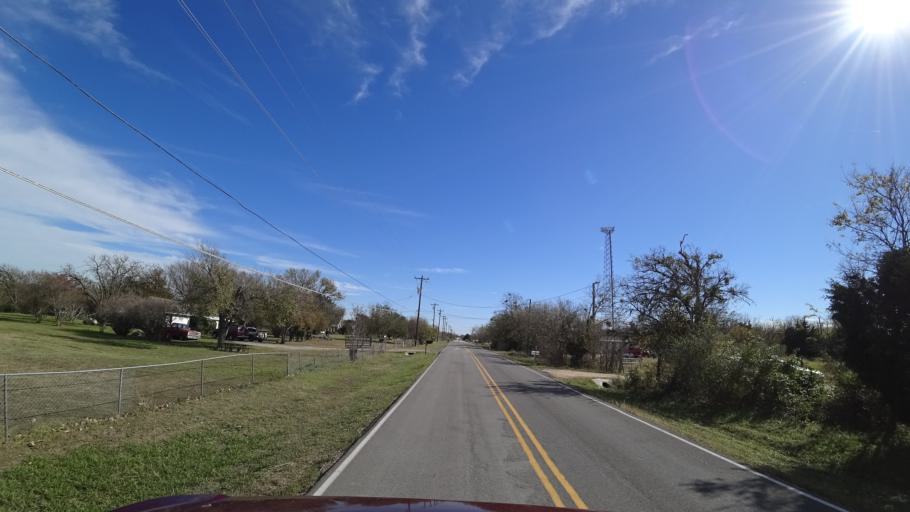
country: US
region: Texas
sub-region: Travis County
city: Onion Creek
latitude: 30.1158
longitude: -97.7043
